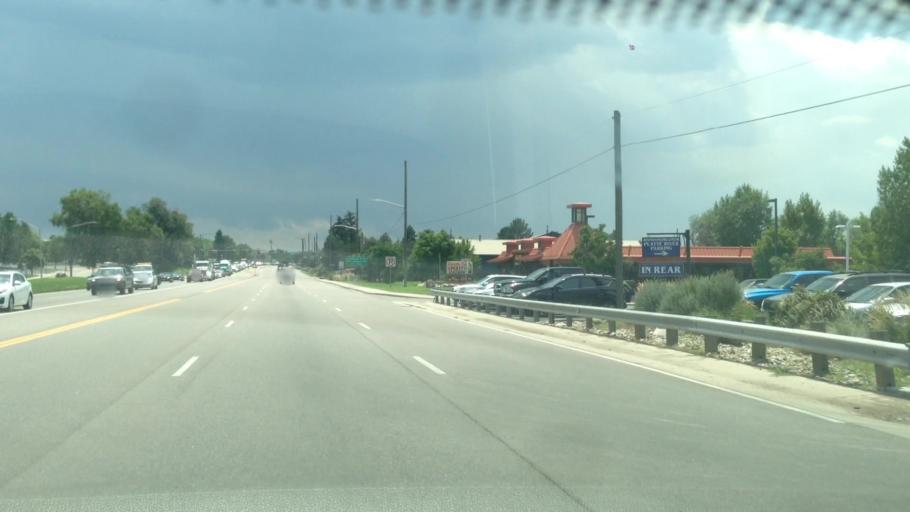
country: US
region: Colorado
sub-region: Arapahoe County
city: Littleton
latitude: 39.6080
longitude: -105.0211
